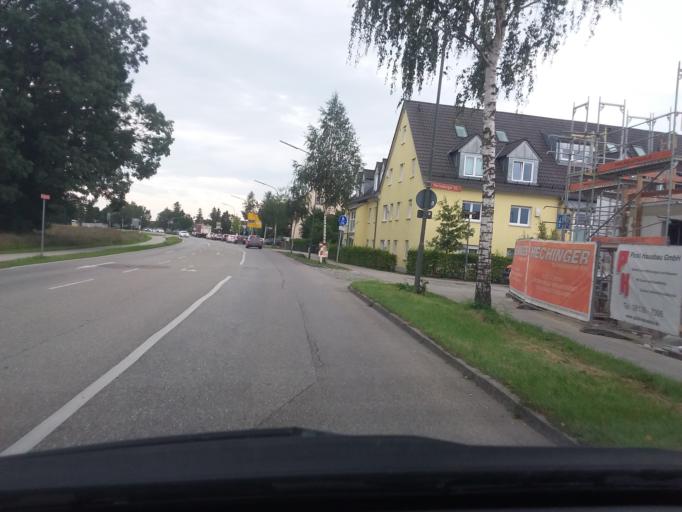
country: DE
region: Bavaria
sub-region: Upper Bavaria
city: Hebertshausen
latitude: 48.2577
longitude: 11.4698
